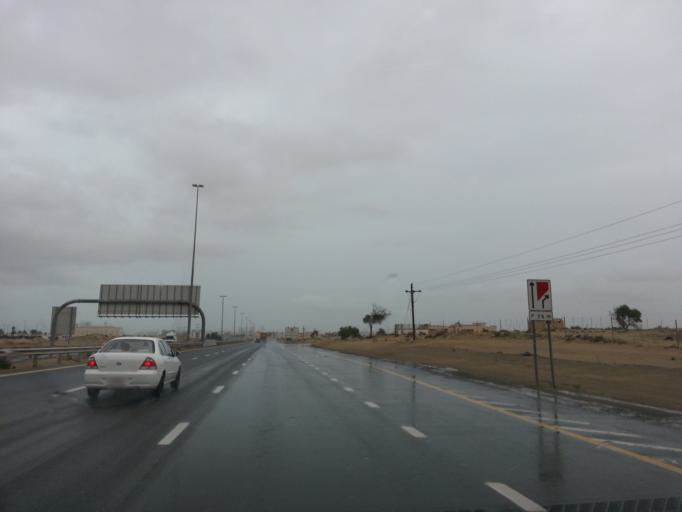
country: AE
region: Dubai
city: Dubai
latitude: 25.0605
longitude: 55.2215
